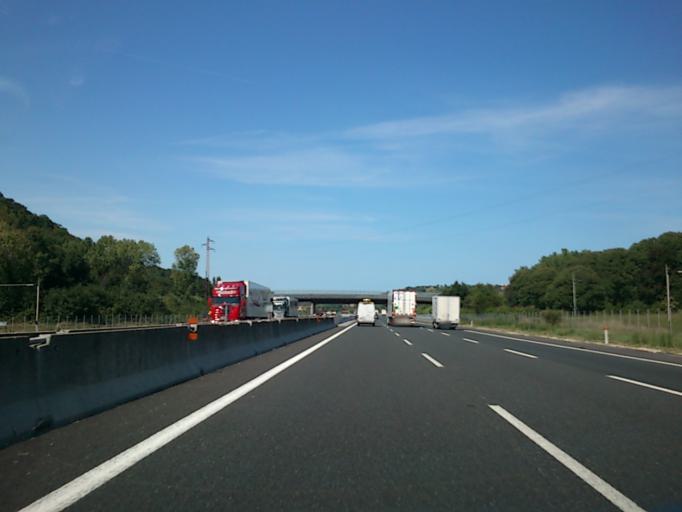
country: IT
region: The Marches
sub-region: Provincia di Pesaro e Urbino
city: Gradara
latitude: 43.9394
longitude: 12.7834
